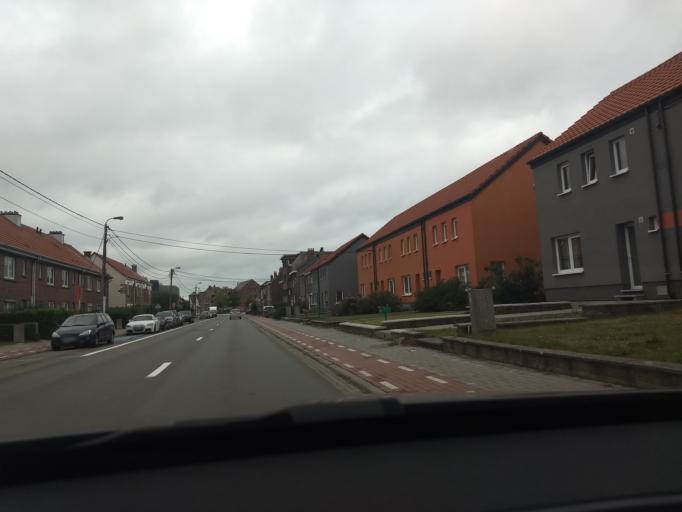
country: BE
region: Wallonia
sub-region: Province du Brabant Wallon
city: Braine-l'Alleud
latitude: 50.6717
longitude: 4.3853
